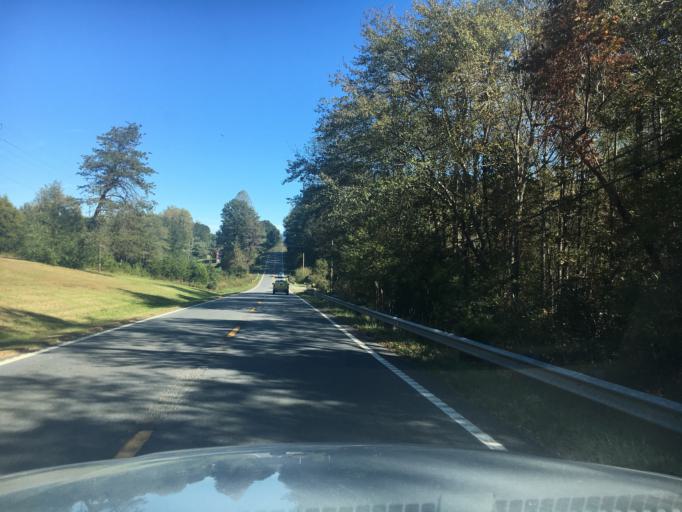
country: US
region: North Carolina
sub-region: Rutherford County
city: Spindale
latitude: 35.4181
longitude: -81.9100
